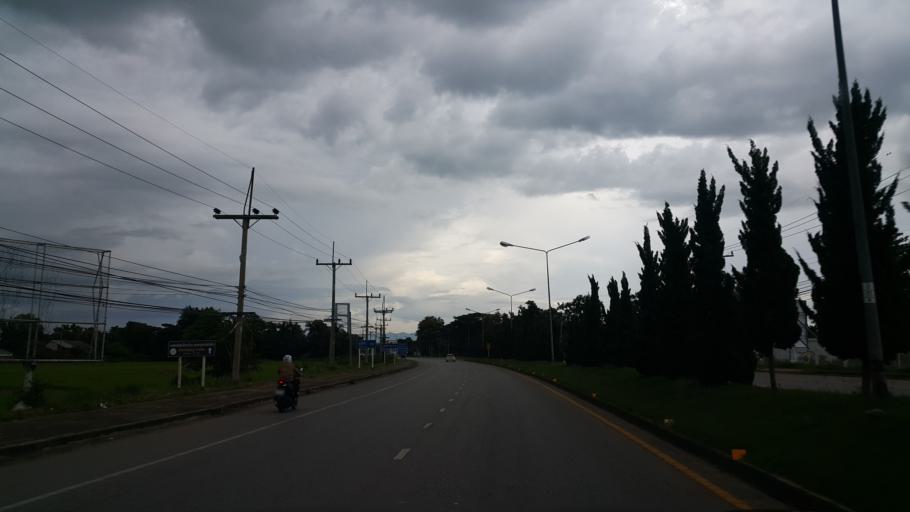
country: TH
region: Phayao
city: Phayao
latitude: 19.1410
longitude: 99.9149
